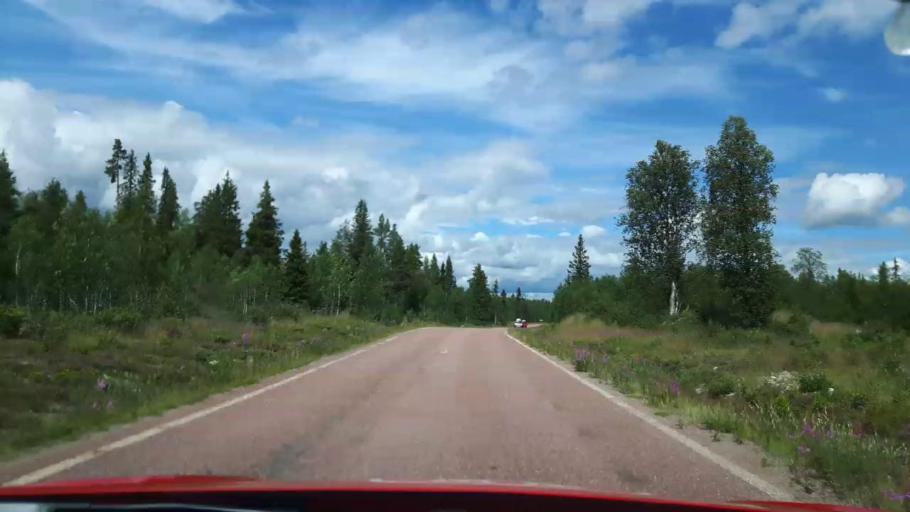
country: NO
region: Hedmark
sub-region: Trysil
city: Innbygda
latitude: 62.0063
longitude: 12.9756
